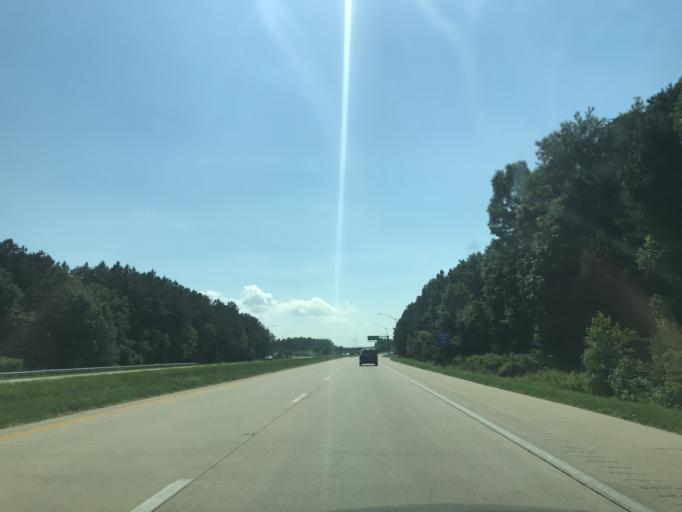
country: US
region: Maryland
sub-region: Wicomico County
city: Salisbury
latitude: 38.4035
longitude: -75.6122
